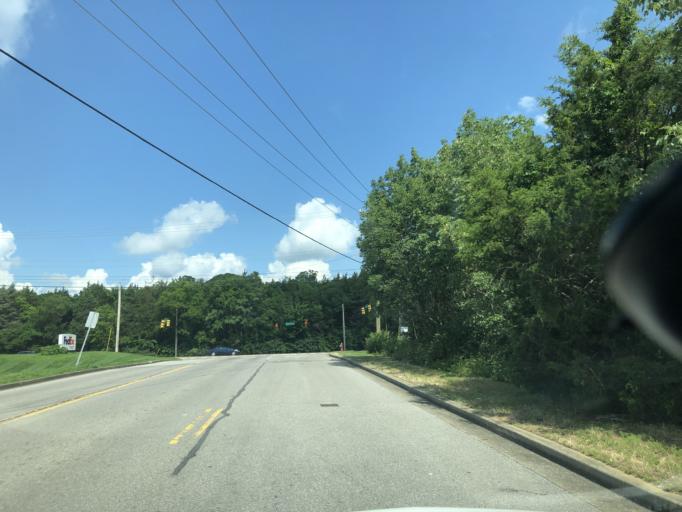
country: US
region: Tennessee
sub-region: Rutherford County
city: La Vergne
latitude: 36.0299
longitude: -86.6116
